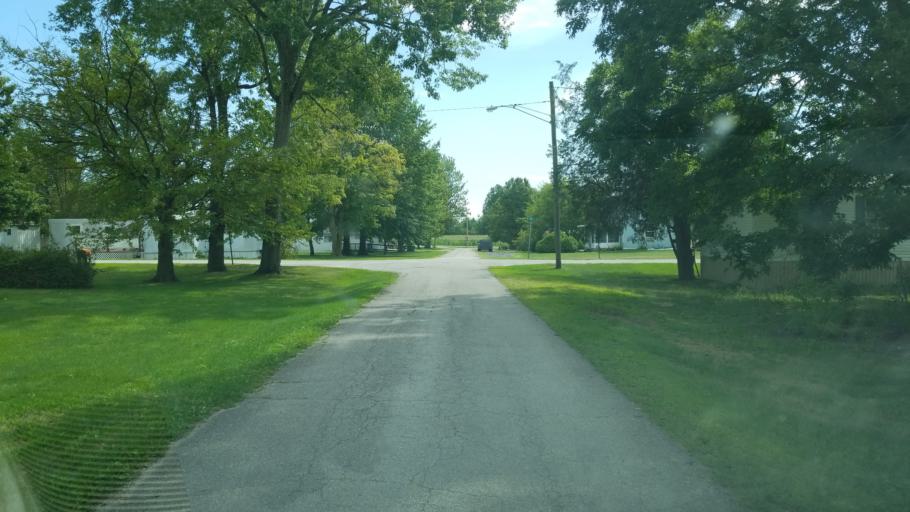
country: US
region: Ohio
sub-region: Union County
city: Richwood
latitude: 40.5836
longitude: -83.3172
